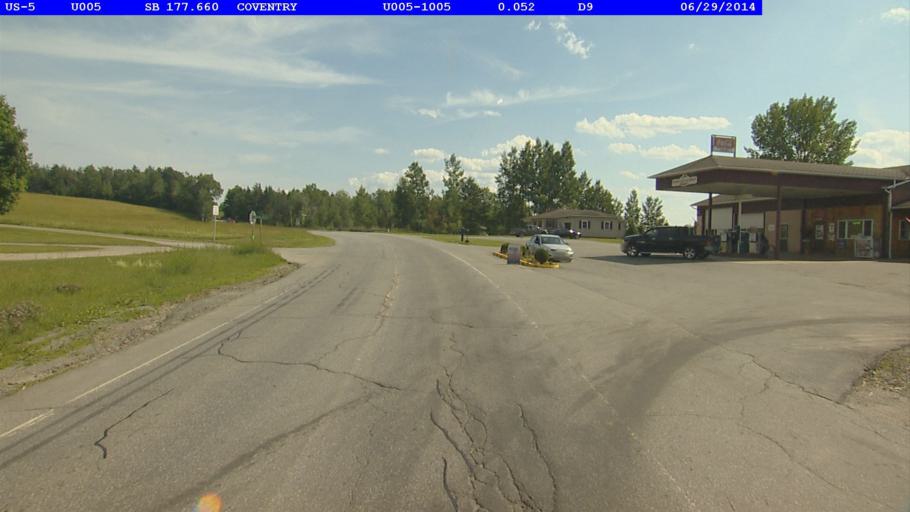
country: US
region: Vermont
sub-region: Orleans County
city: Newport
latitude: 44.8604
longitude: -72.2681
